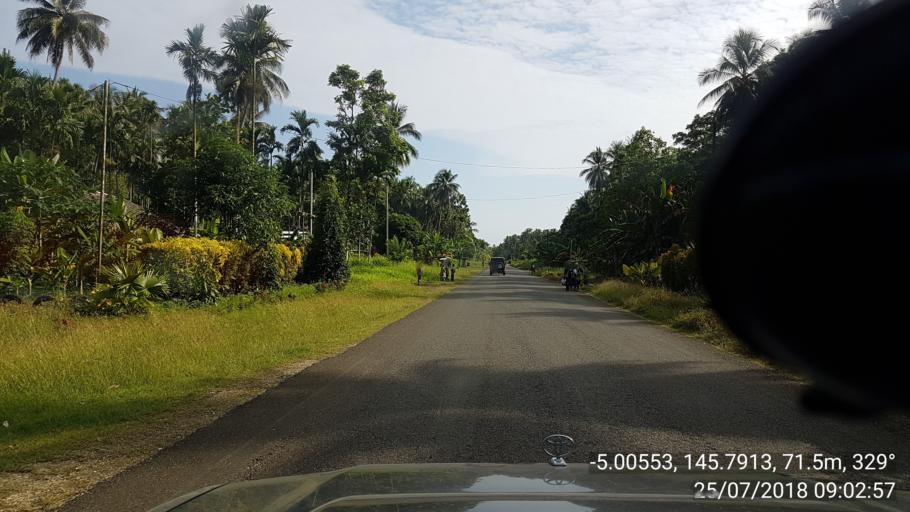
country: PG
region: Madang
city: Madang
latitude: -5.0056
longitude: 145.7915
